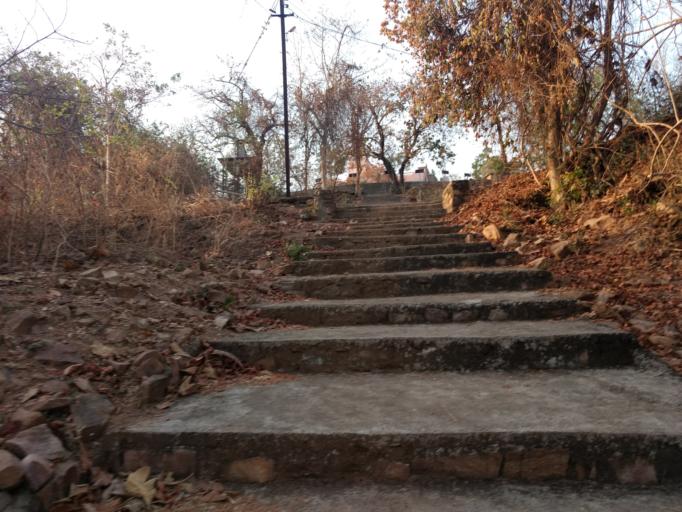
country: IN
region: Maharashtra
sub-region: Bhandara
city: Pauni
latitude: 20.5858
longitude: 79.7839
